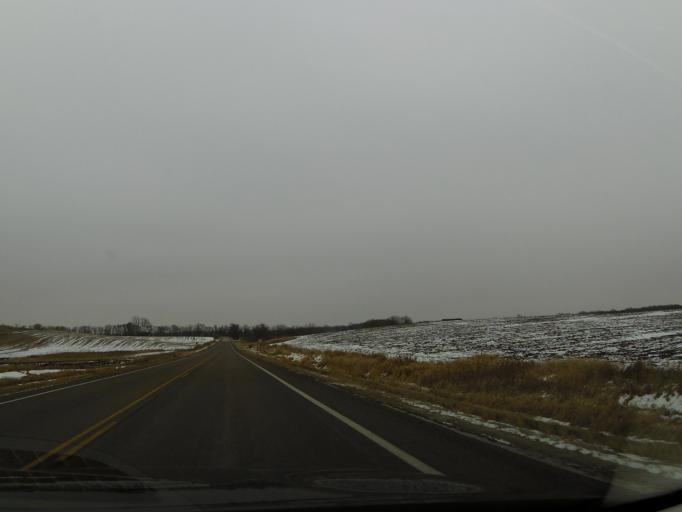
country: US
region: Minnesota
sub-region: Scott County
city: Prior Lake
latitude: 44.6305
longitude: -93.4895
